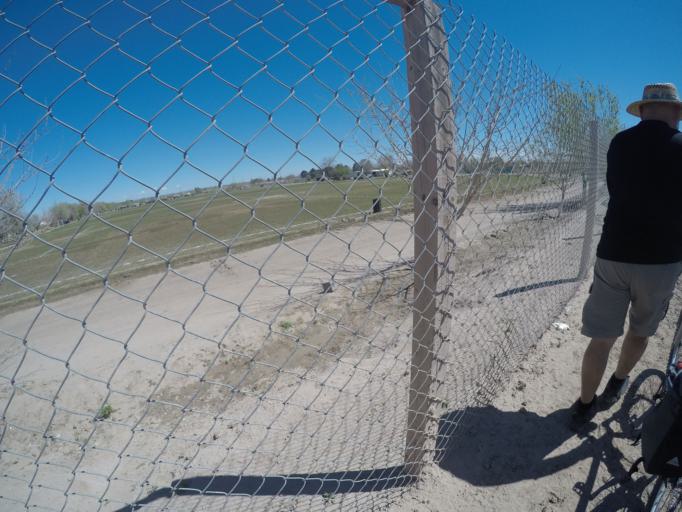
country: US
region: Texas
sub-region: El Paso County
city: Socorro Mission Number 1 Colonia
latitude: 31.6098
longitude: -106.3136
